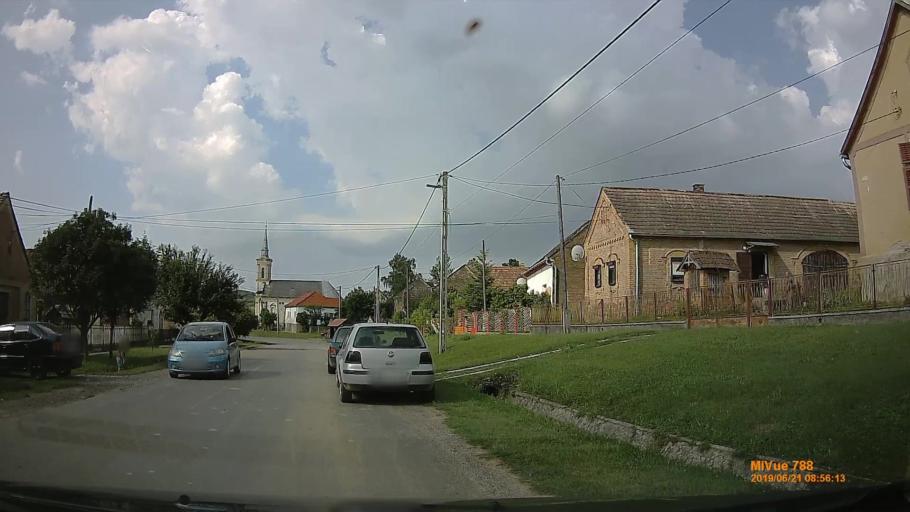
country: HU
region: Baranya
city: Buekkoesd
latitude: 46.1583
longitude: 17.8750
